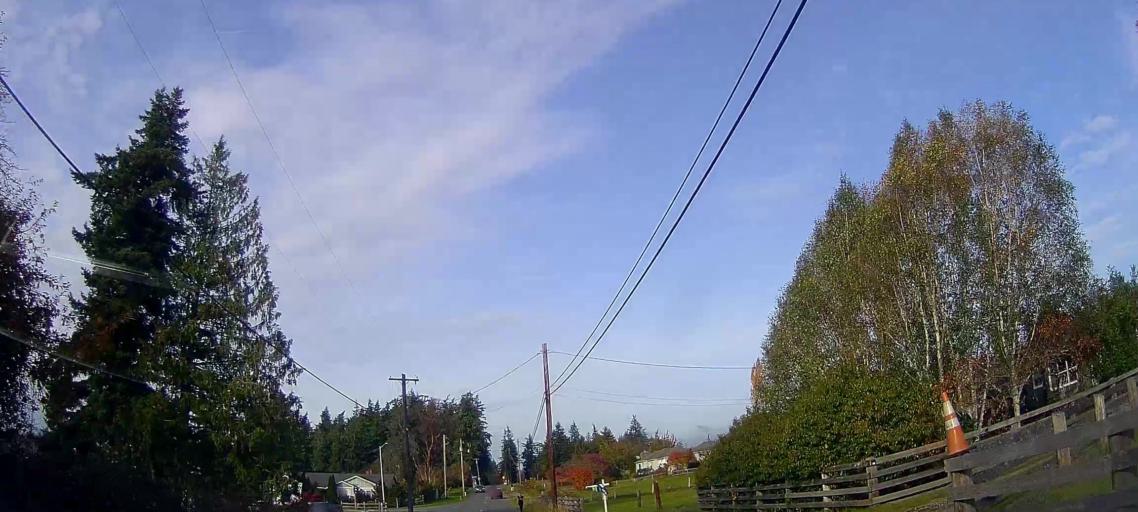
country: US
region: Washington
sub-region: Snohomish County
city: Stanwood
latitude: 48.2527
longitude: -122.3414
